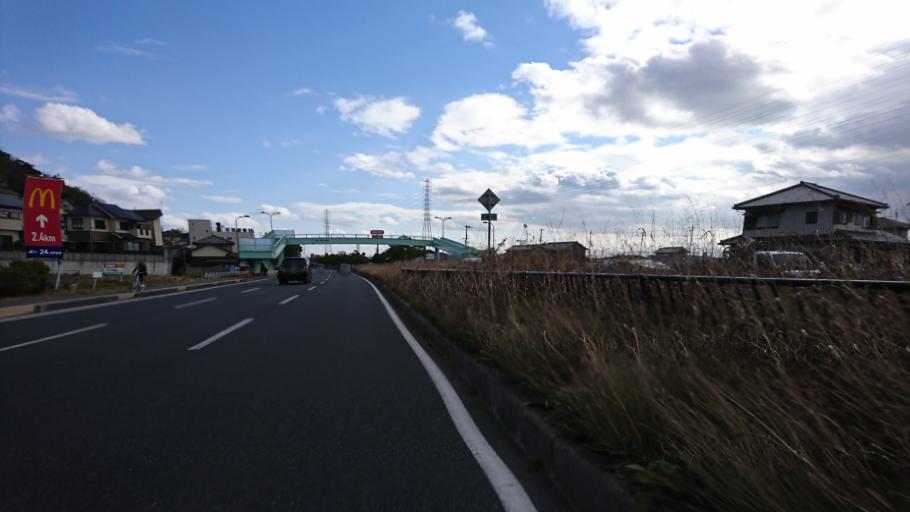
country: JP
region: Hyogo
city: Kakogawacho-honmachi
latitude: 34.7763
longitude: 134.7936
